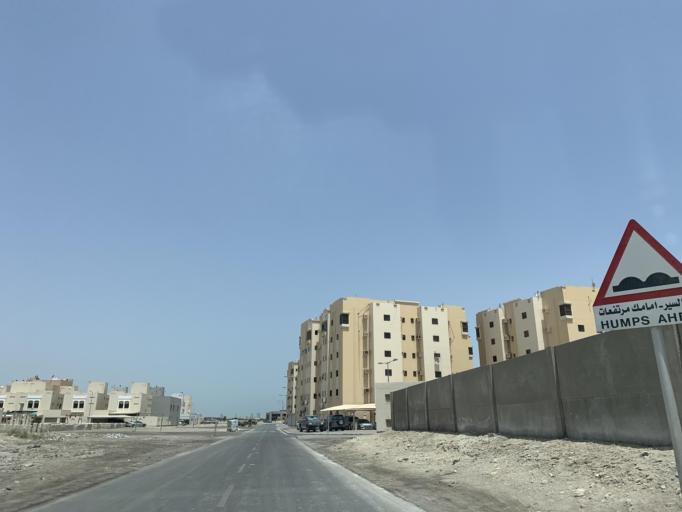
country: BH
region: Northern
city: Sitrah
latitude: 26.1407
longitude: 50.5957
